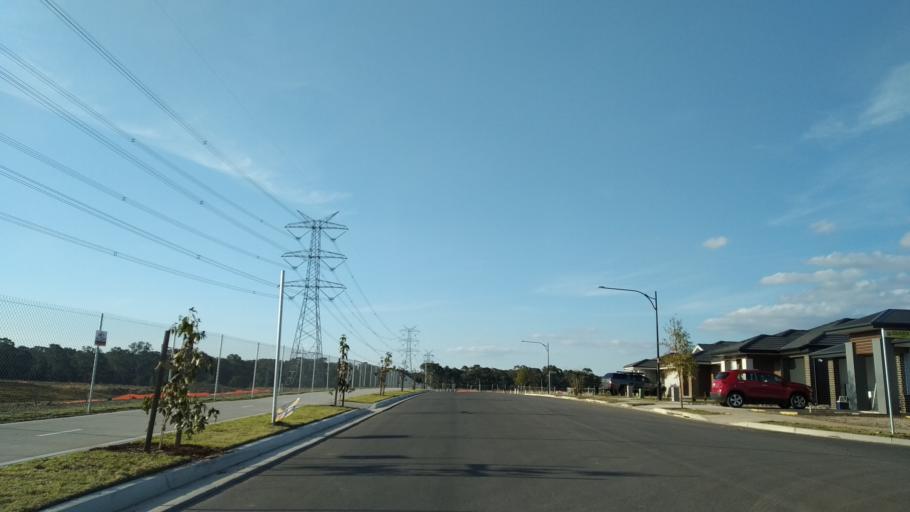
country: AU
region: New South Wales
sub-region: Penrith Municipality
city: Werrington County
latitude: -33.7292
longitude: 150.7550
